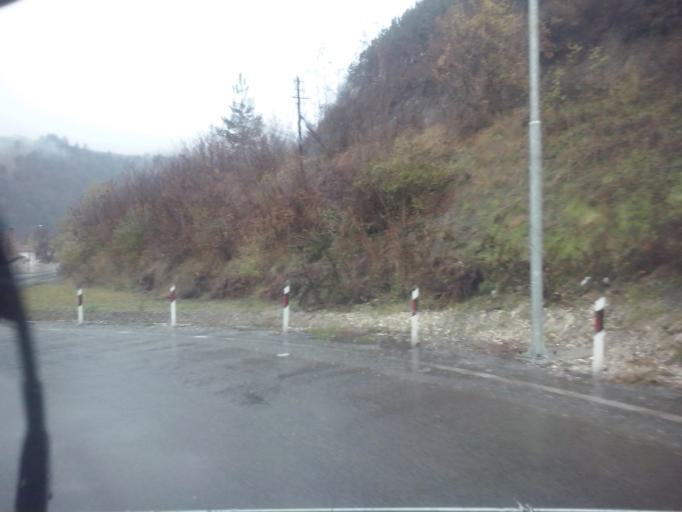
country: RS
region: Central Serbia
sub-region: Raski Okrug
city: Raska
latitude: 43.2878
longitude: 20.6206
